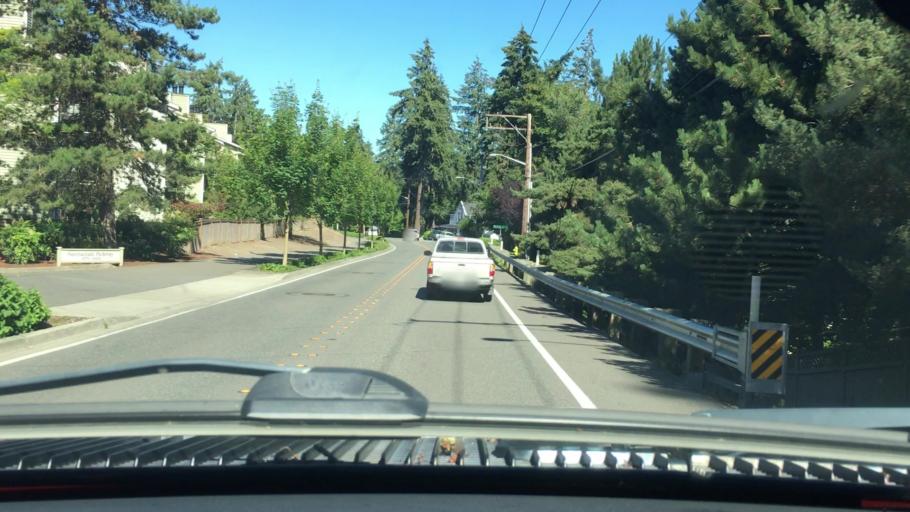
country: US
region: Washington
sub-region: King County
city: West Lake Sammamish
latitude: 47.5704
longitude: -122.1018
